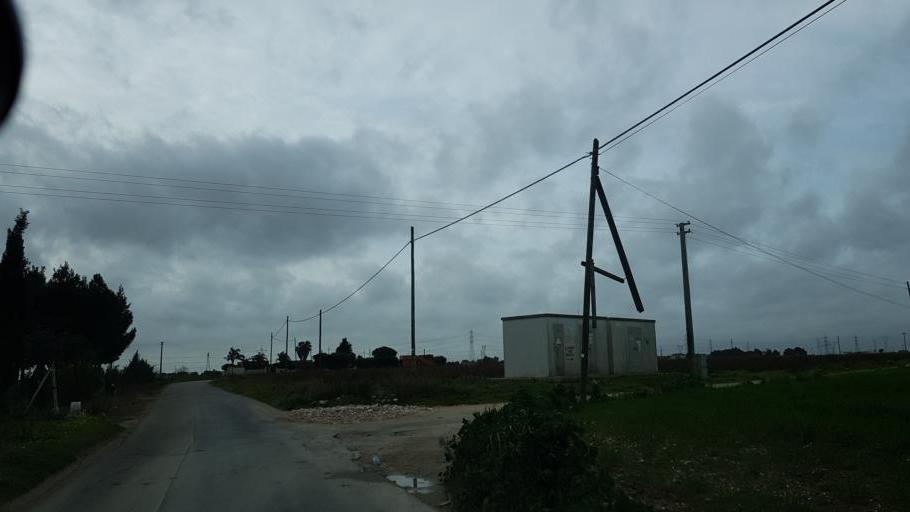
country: IT
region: Apulia
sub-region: Provincia di Brindisi
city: Brindisi
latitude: 40.6081
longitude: 17.9256
